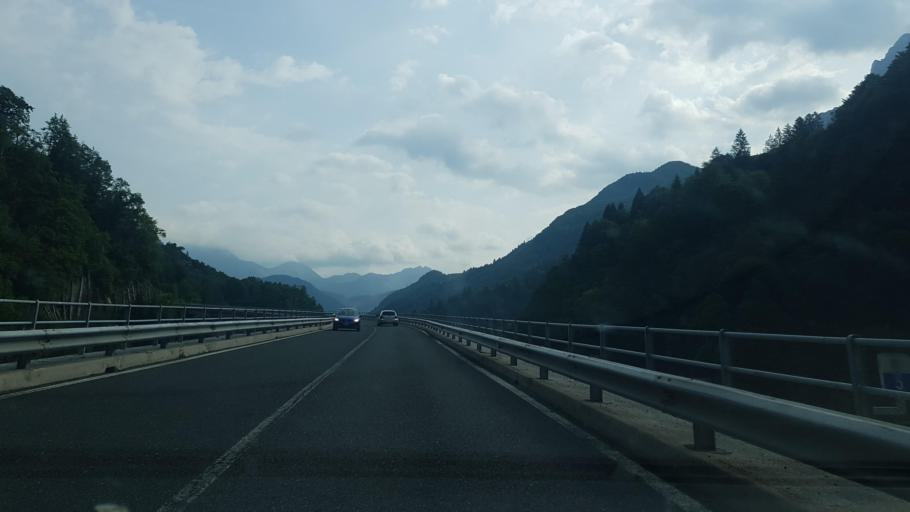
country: IT
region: Friuli Venezia Giulia
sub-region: Provincia di Udine
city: Paularo
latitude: 46.4825
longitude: 13.0914
